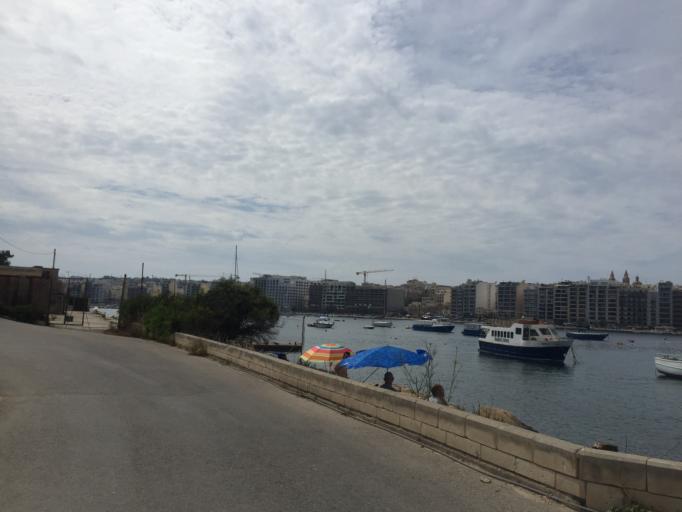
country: MT
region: Tas-Sliema
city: Sliema
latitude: 35.9052
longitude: 14.5054
